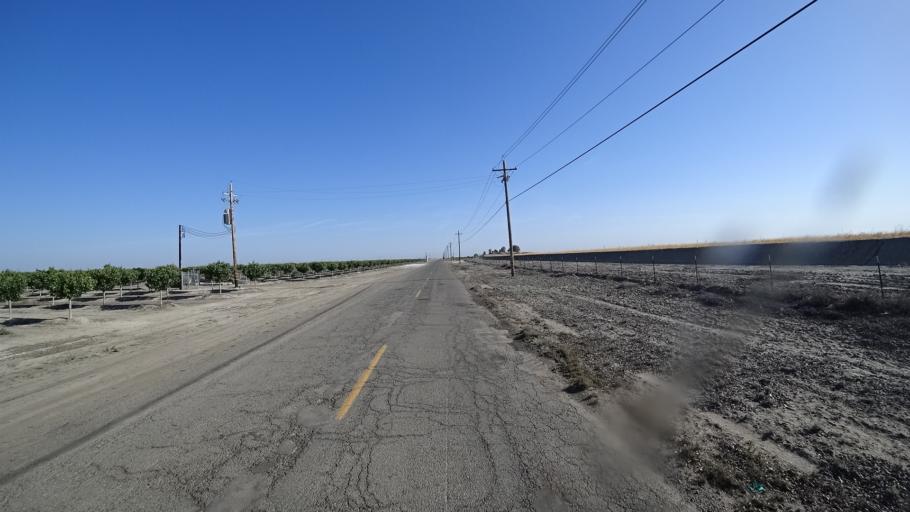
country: US
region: California
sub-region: Kings County
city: Corcoran
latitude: 36.1287
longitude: -119.5543
